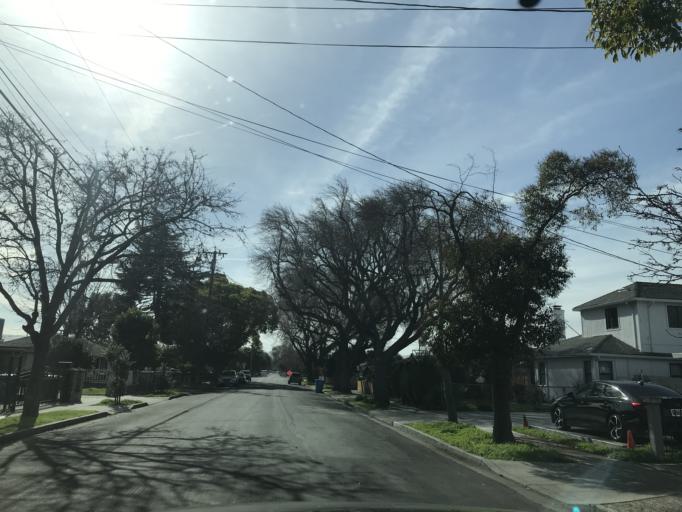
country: US
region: California
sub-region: San Mateo County
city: East Palo Alto
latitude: 37.4773
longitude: -122.1536
